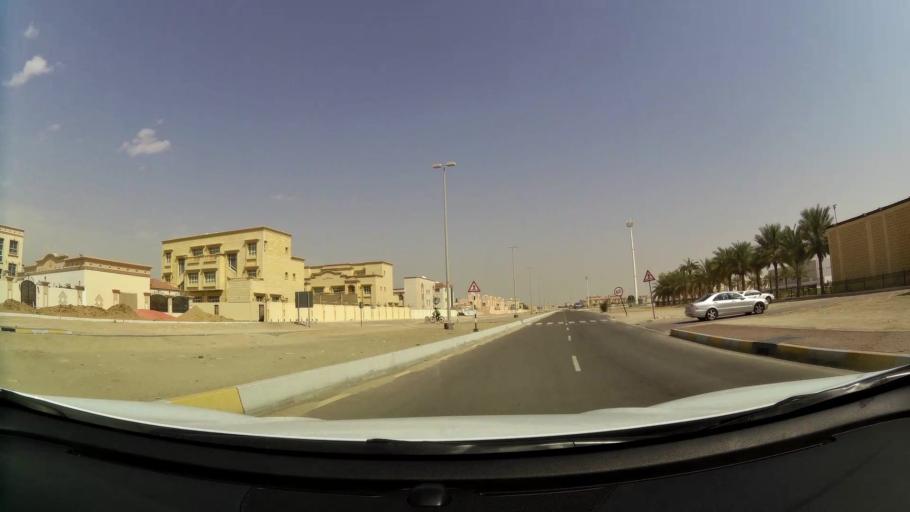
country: AE
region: Abu Dhabi
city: Abu Dhabi
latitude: 24.3412
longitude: 54.5546
